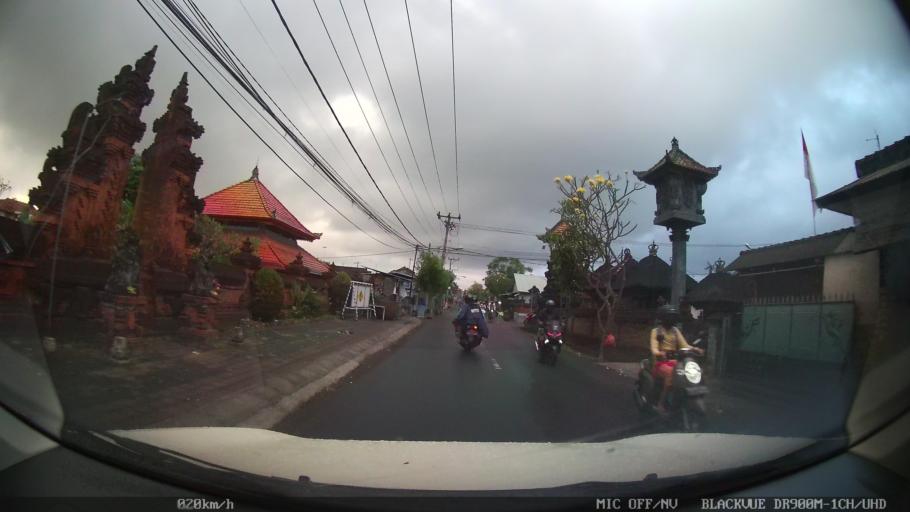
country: ID
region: Bali
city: Banjar Batur
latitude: -8.6063
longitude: 115.2210
